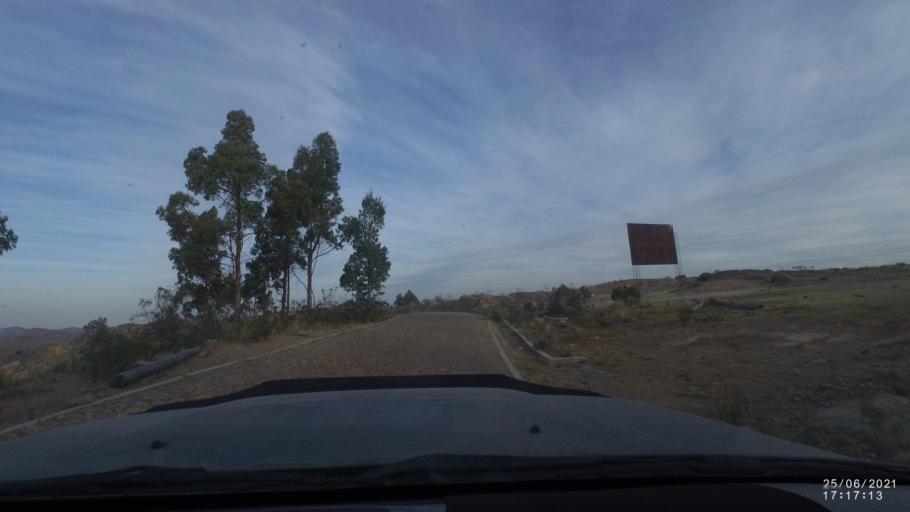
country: BO
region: Cochabamba
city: Arani
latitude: -17.8864
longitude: -65.6998
